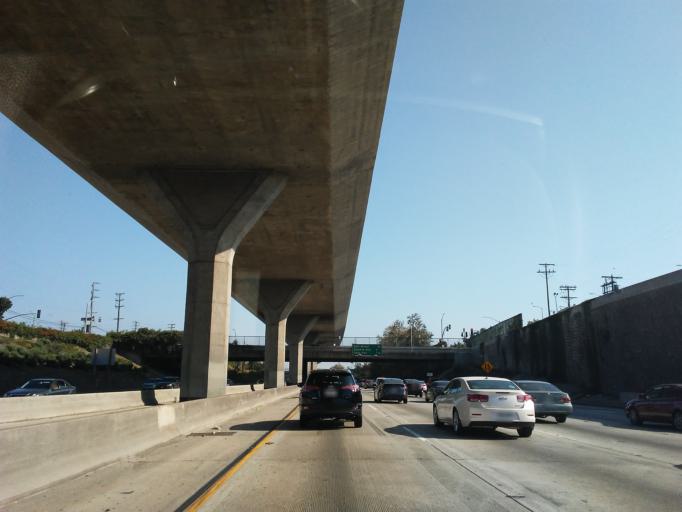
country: US
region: California
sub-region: Los Angeles County
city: Florence-Graham
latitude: 34.0050
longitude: -118.2812
